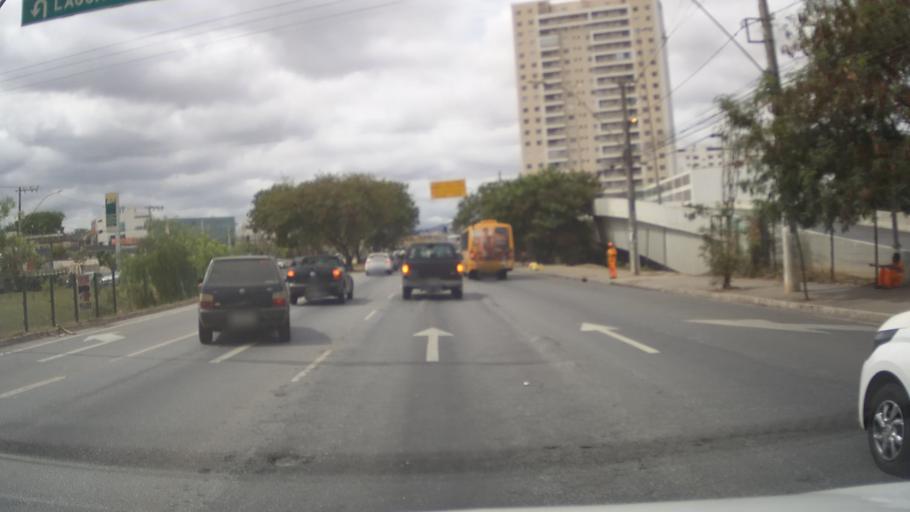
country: BR
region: Minas Gerais
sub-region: Belo Horizonte
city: Belo Horizonte
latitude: -19.8215
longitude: -43.9458
